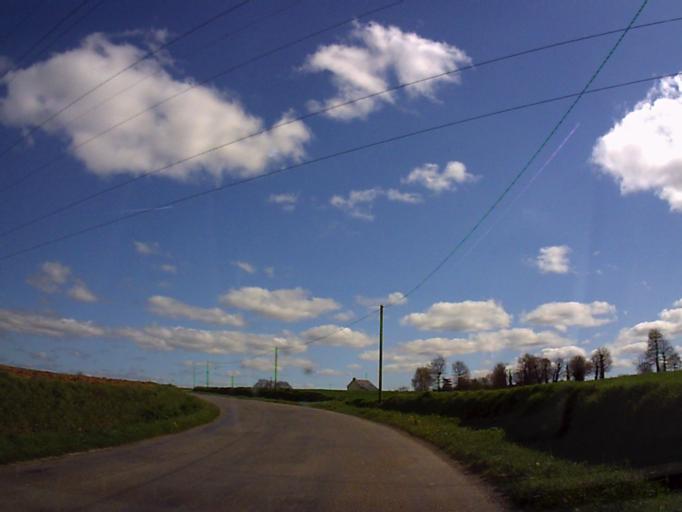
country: FR
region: Brittany
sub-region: Departement d'Ille-et-Vilaine
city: Saint-Meen-le-Grand
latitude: 48.1462
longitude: -2.1572
